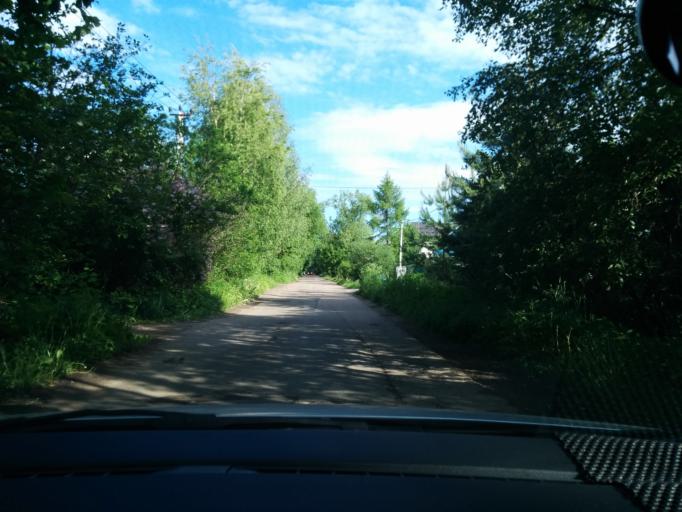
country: RU
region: Moskovskaya
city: Lugovaya
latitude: 56.0541
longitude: 37.4849
